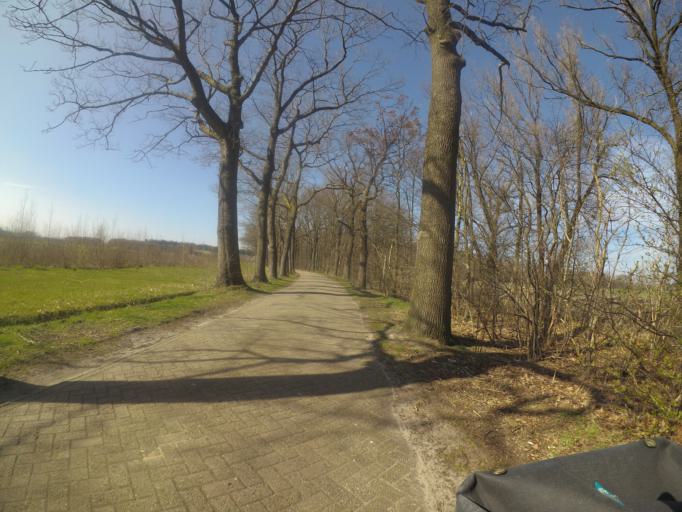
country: NL
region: North Brabant
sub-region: Gemeente Oirschot
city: Oostelbeers
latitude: 51.4773
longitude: 5.2617
